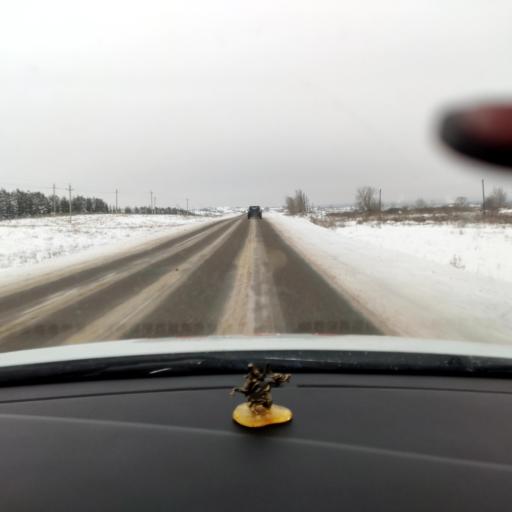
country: RU
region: Tatarstan
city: Vysokaya Gora
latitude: 56.0094
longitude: 49.2897
